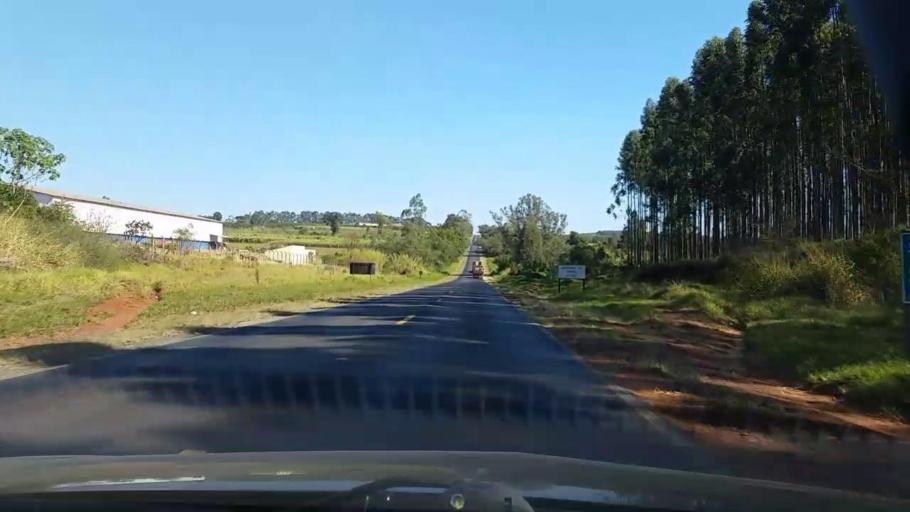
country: BR
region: Sao Paulo
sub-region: Sao Manuel
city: Sao Manuel
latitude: -22.8084
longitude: -48.6737
